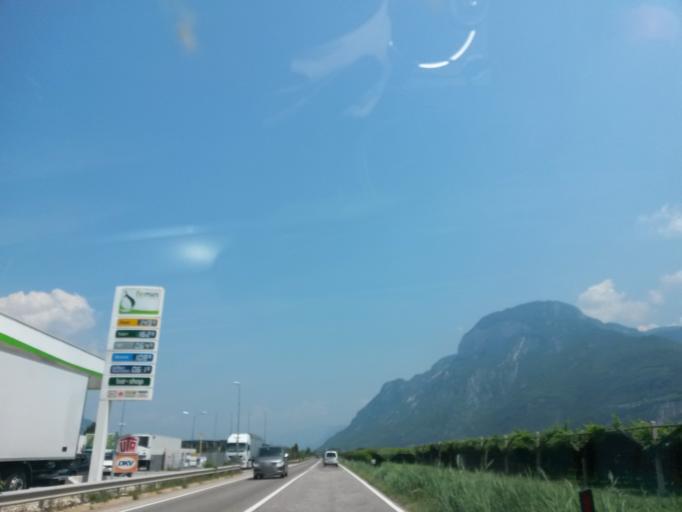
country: IT
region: Trentino-Alto Adige
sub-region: Bolzano
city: Salorno
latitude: 46.2455
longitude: 11.2128
